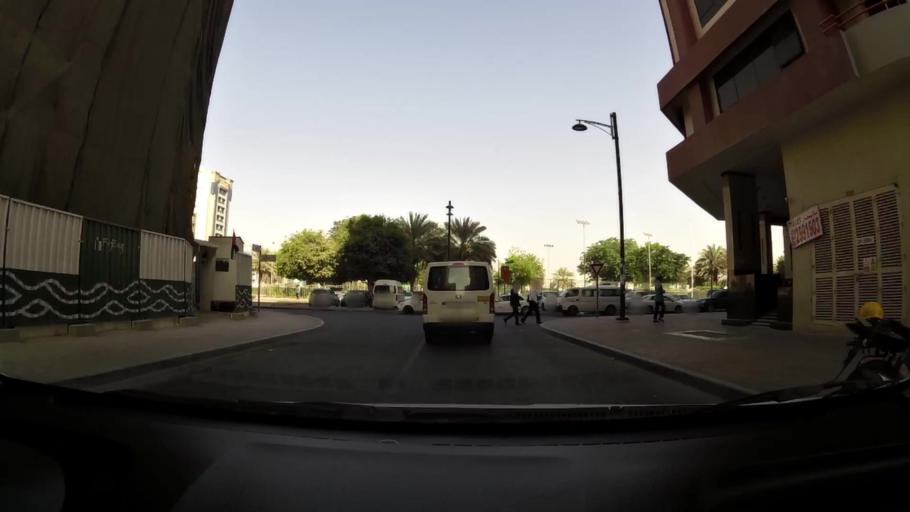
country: AE
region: Ash Shariqah
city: Sharjah
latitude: 25.2918
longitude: 55.3809
